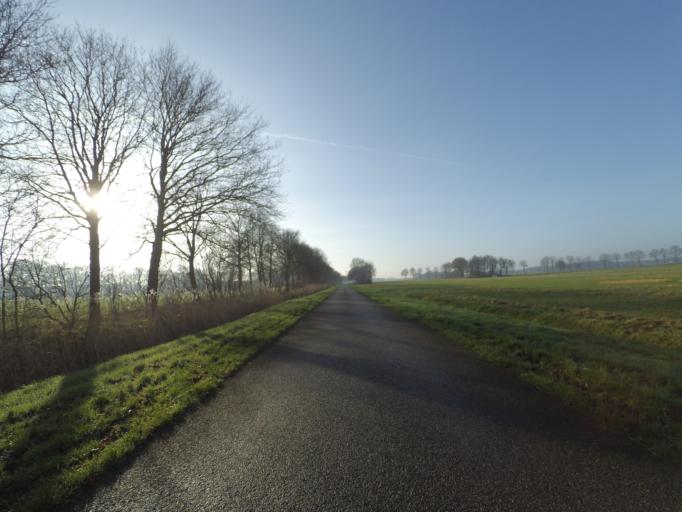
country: NL
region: Drenthe
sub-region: Gemeente Assen
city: Assen
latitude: 52.8551
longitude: 6.6392
